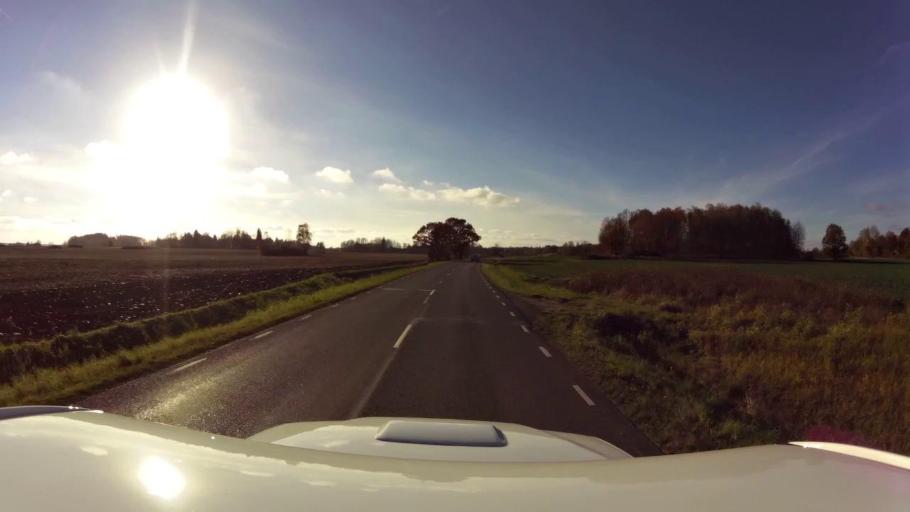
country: SE
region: OEstergoetland
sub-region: Linkopings Kommun
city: Malmslatt
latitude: 58.3488
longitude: 15.5419
